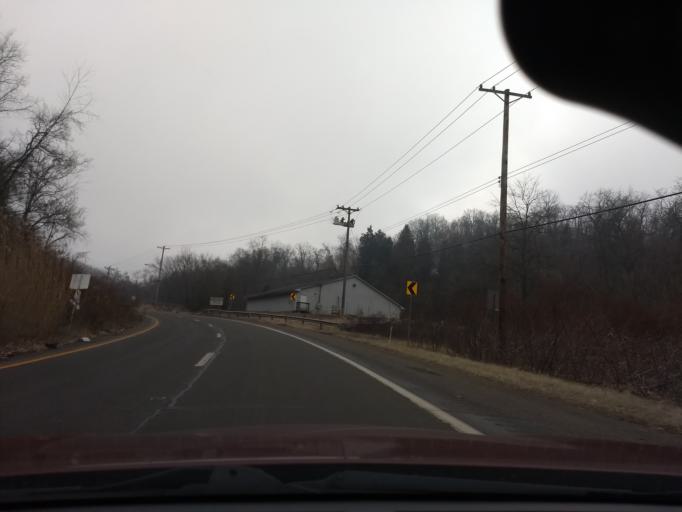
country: US
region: Pennsylvania
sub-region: Allegheny County
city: East Pittsburgh
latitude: 40.3871
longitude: -79.8298
